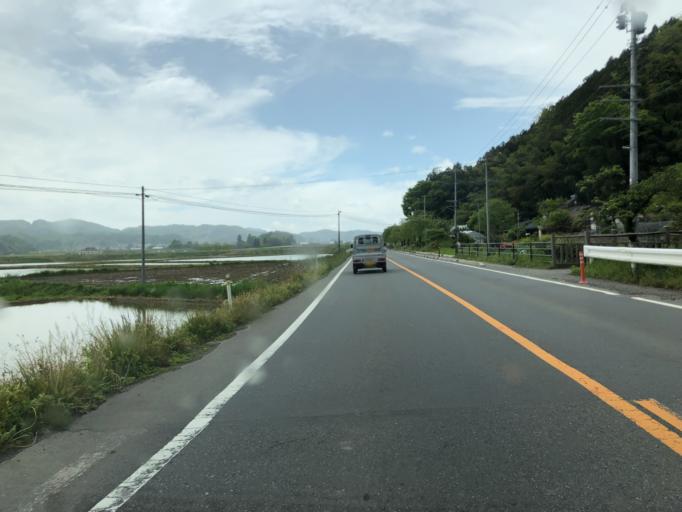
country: JP
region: Fukushima
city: Ishikawa
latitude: 37.1285
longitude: 140.3063
